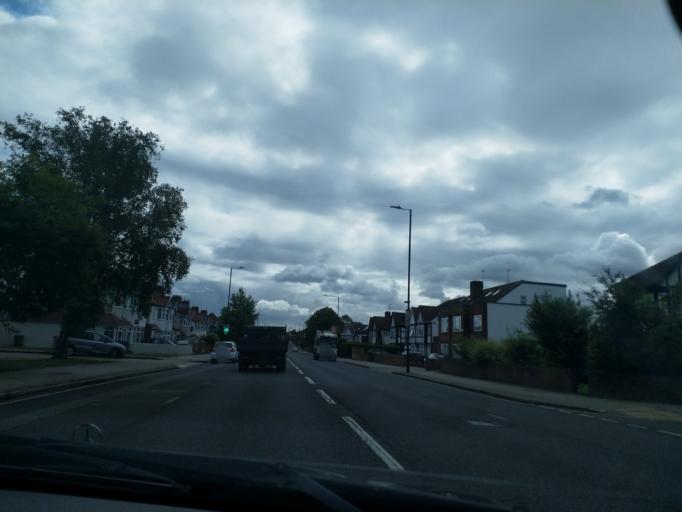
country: GB
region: England
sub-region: Greater London
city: Edgware
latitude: 51.5864
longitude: -0.2923
